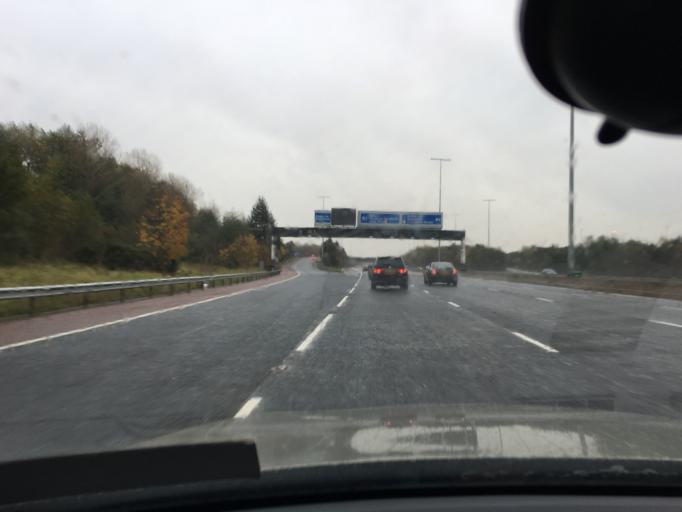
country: GB
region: Northern Ireland
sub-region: Newtownabbey District
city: Newtownabbey
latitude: 54.6343
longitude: -5.9191
